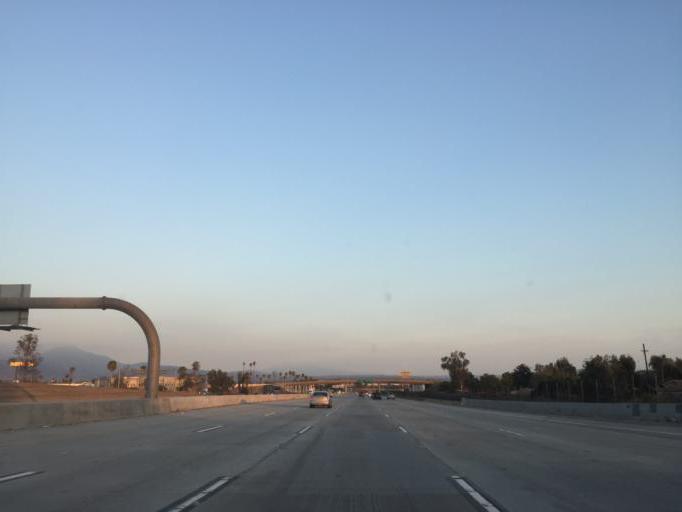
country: US
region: California
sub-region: San Bernardino County
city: San Bernardino
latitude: 34.1358
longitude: -117.3129
